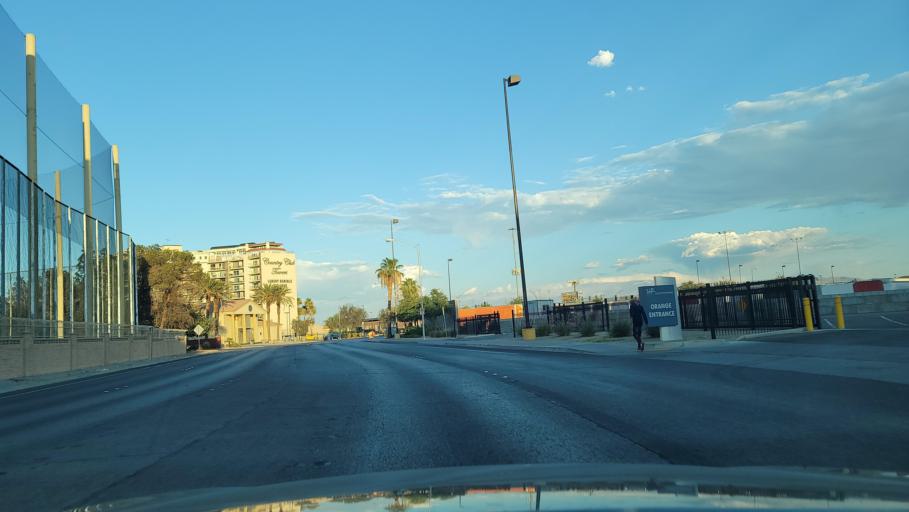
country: US
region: Nevada
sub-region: Clark County
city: Winchester
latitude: 36.1313
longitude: -115.1474
